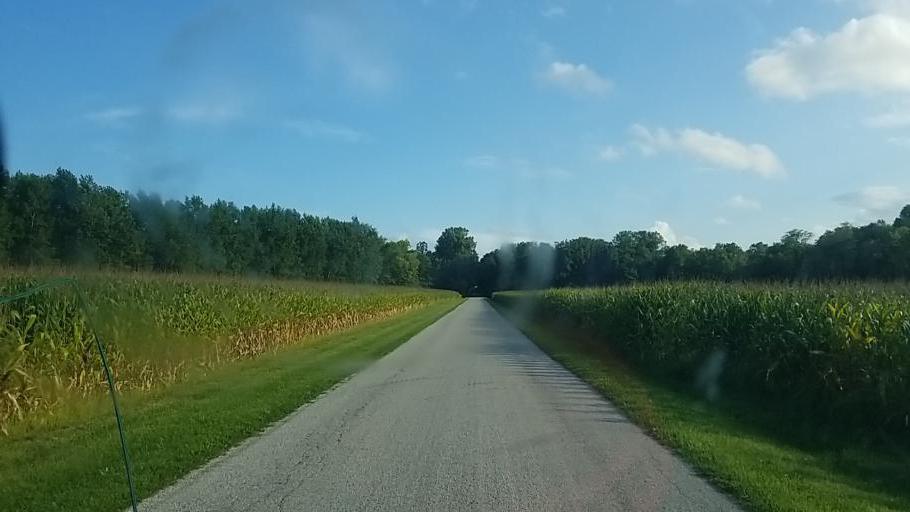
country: US
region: Ohio
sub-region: Crawford County
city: Bucyrus
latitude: 40.7734
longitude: -83.0552
